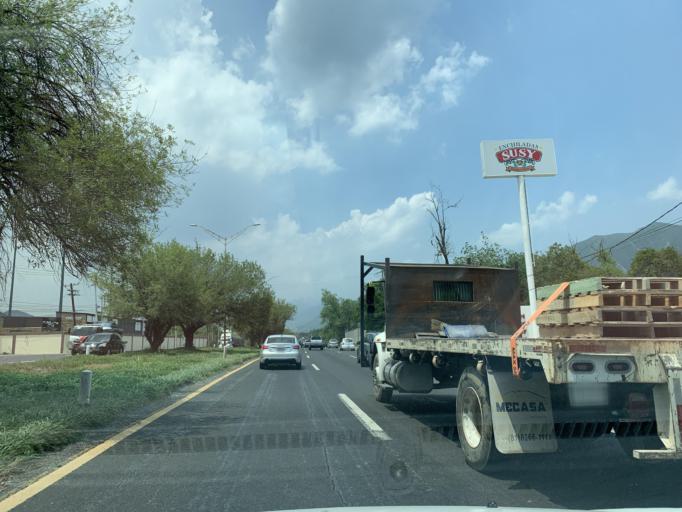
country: MX
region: Nuevo Leon
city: Santiago
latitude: 25.4982
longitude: -100.1900
